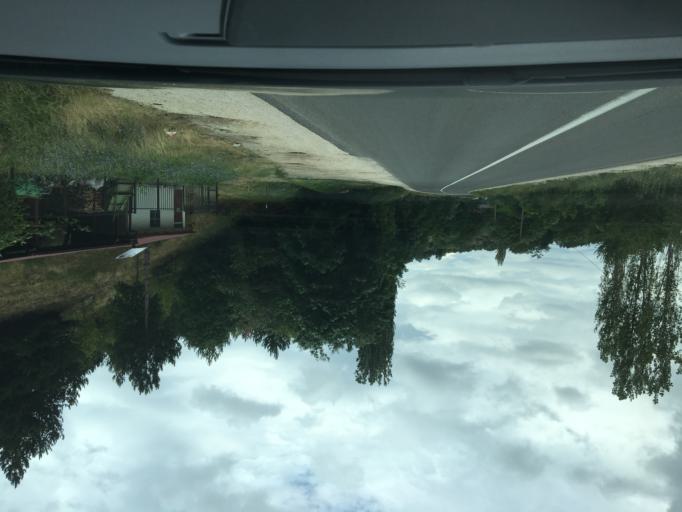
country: MK
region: Kriva Palanka
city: Kriva Palanka
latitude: 42.1973
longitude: 22.3149
